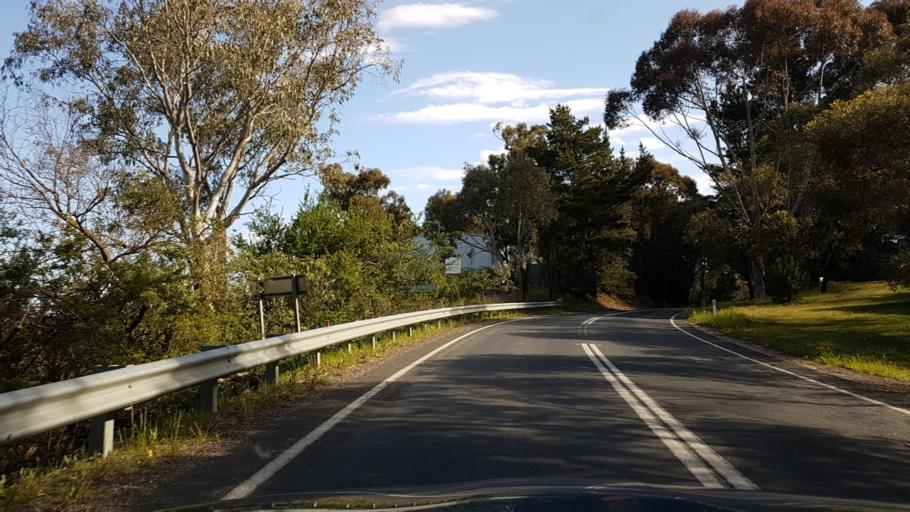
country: AU
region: South Australia
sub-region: Adelaide Hills
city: Lobethal
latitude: -34.8785
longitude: 138.8919
